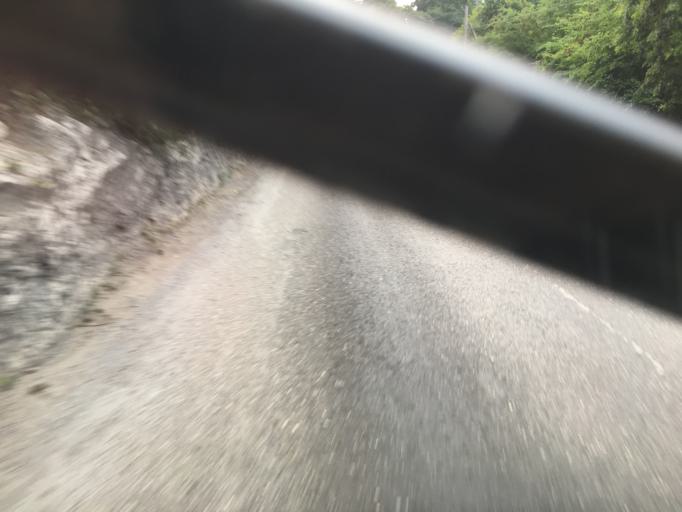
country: JM
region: Saint James
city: Montego Bay
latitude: 18.4908
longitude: -77.9208
